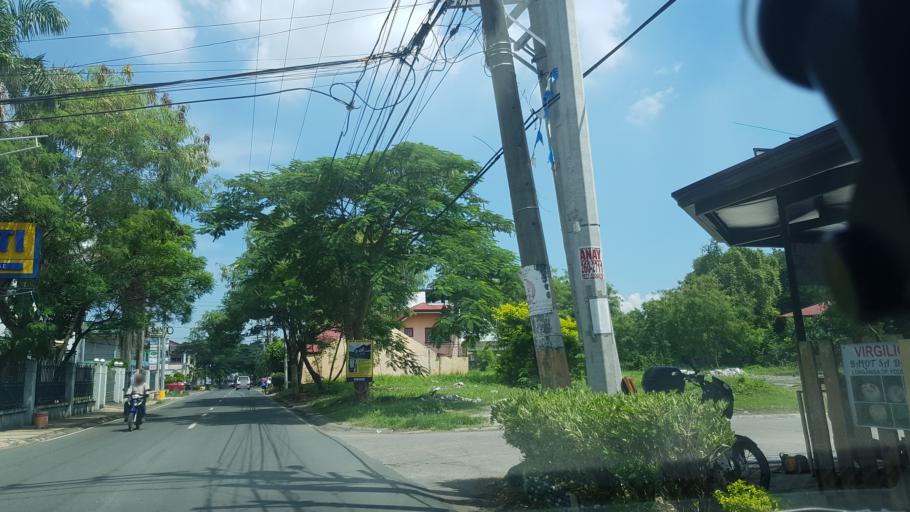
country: PH
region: Calabarzon
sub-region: Province of Rizal
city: Las Pinas
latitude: 14.4307
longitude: 120.9944
